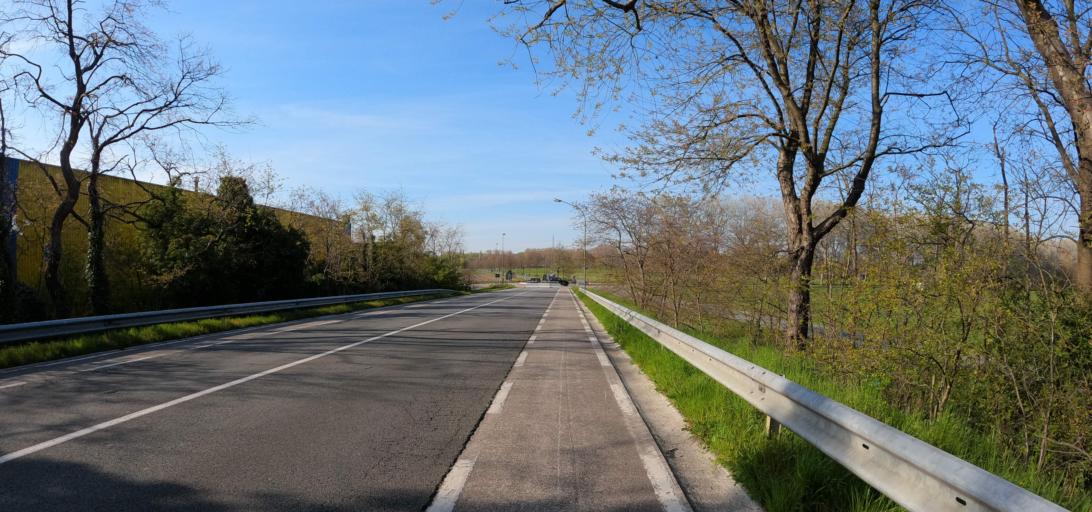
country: BE
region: Flanders
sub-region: Provincie Antwerpen
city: Wommelgem
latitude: 51.2136
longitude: 4.5276
